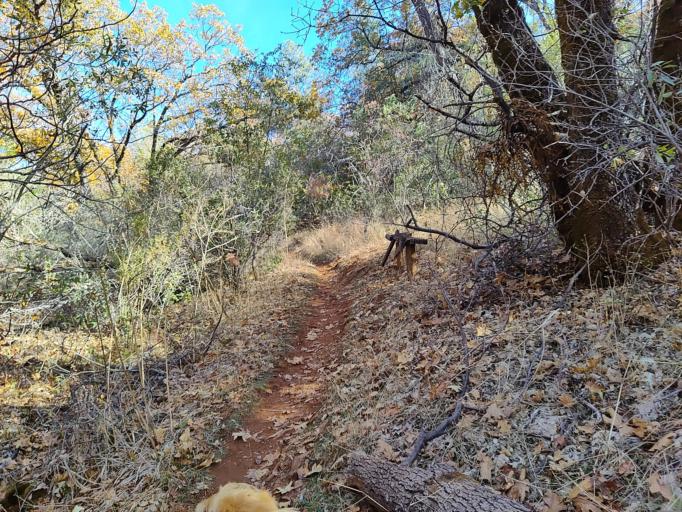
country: US
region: California
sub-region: Placer County
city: Meadow Vista
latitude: 39.0219
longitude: -120.9827
